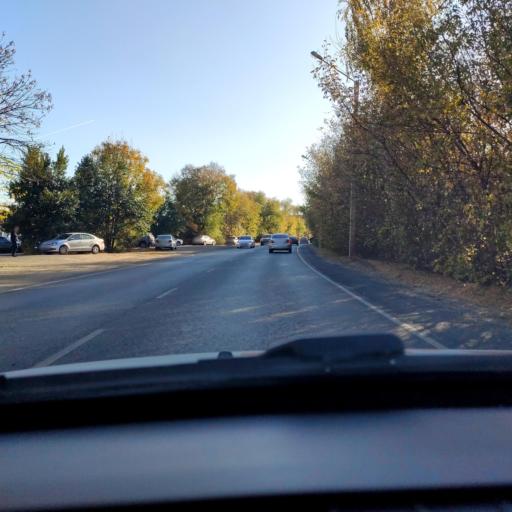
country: RU
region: Voronezj
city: Maslovka
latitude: 51.5890
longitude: 39.1740
